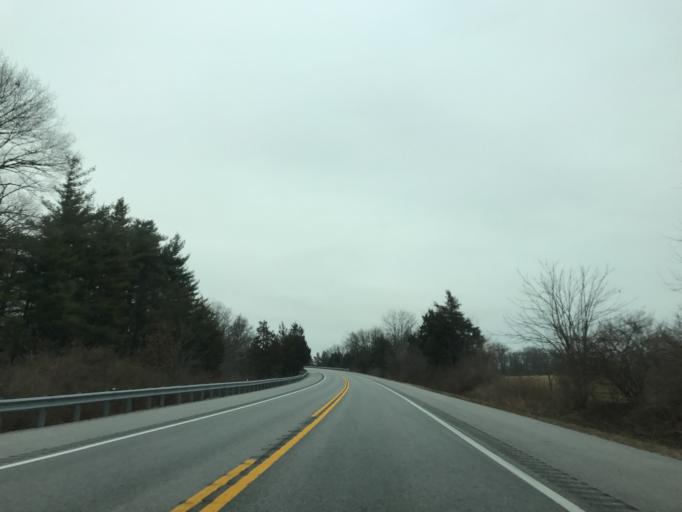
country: US
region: Maryland
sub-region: Carroll County
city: Taneytown
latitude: 39.6375
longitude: -77.1231
